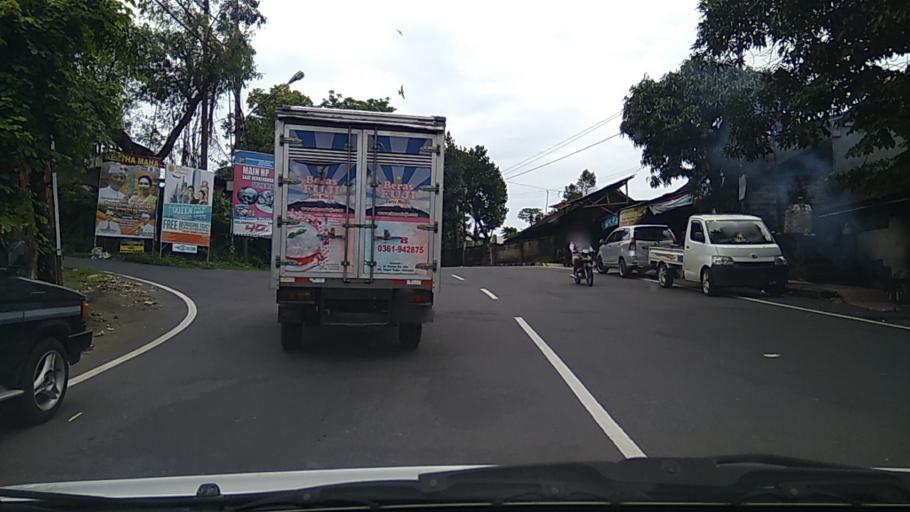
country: ID
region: Bali
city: Banjar Kelodan
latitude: -8.5410
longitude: 115.3348
